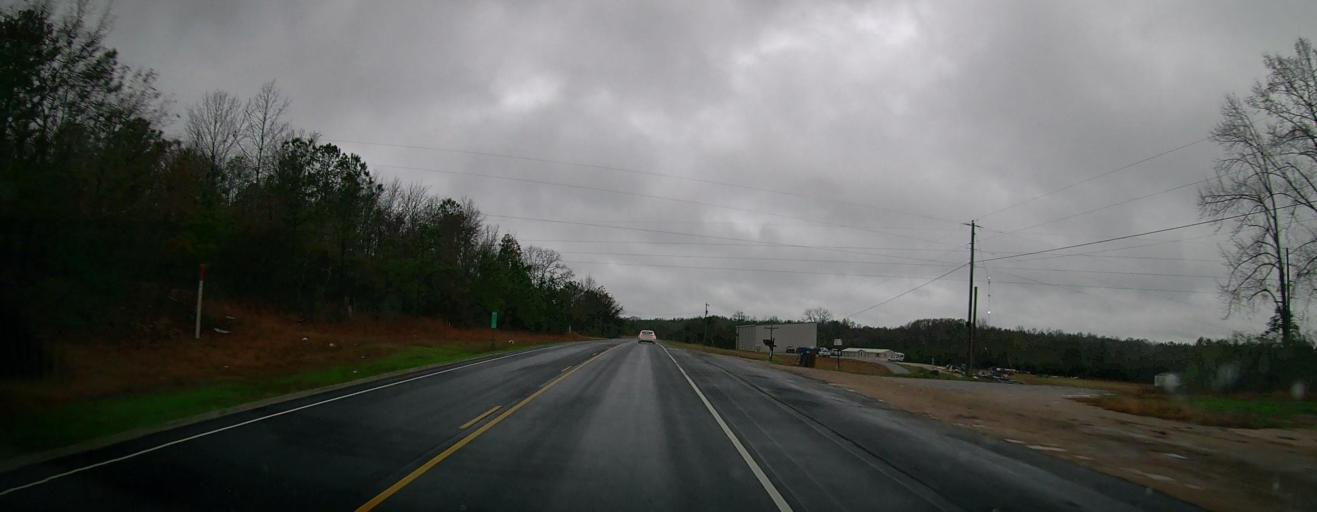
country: US
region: Alabama
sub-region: Chilton County
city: Clanton
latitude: 32.6440
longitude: -86.7590
